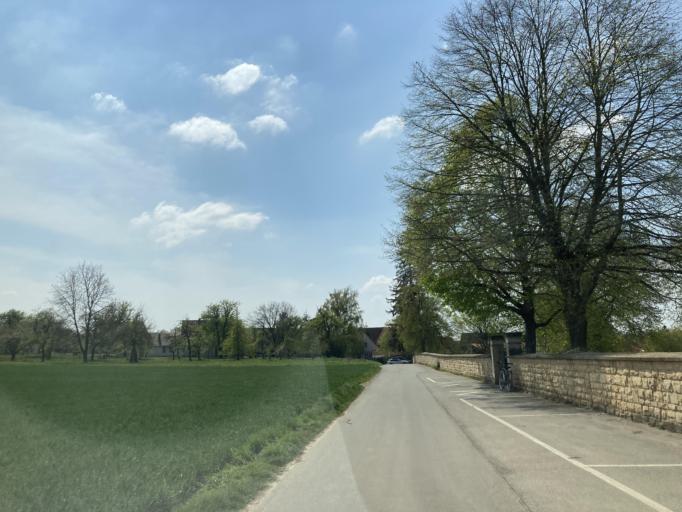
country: DE
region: Baden-Wuerttemberg
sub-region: Tuebingen Region
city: Kusterdingen
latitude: 48.5208
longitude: 9.1252
